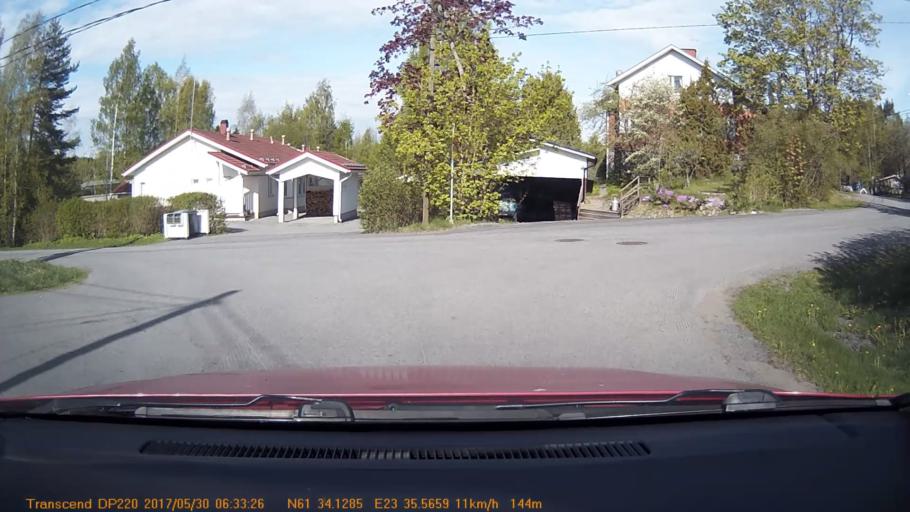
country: FI
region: Pirkanmaa
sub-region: Tampere
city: Yloejaervi
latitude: 61.5688
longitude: 23.5929
